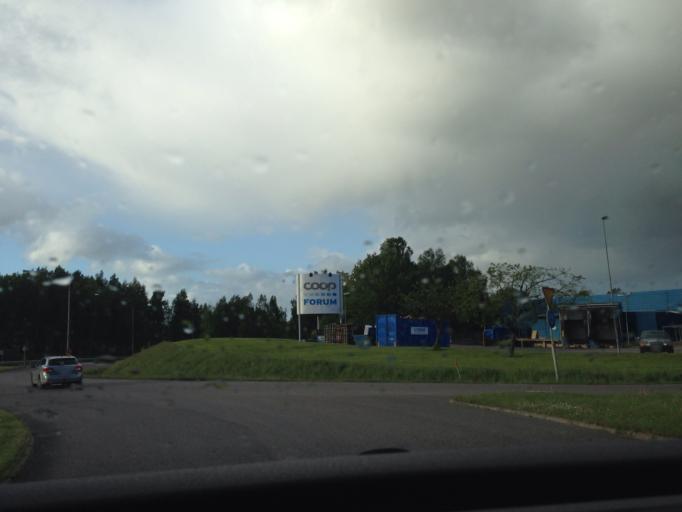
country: SE
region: Vaestra Goetaland
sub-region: Skovde Kommun
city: Skoevde
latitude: 58.4075
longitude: 13.8545
